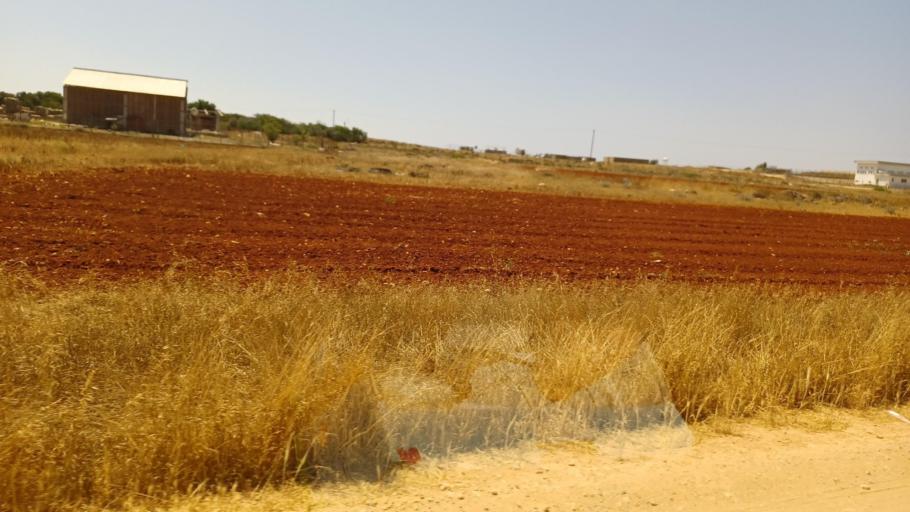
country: CY
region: Ammochostos
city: Liopetri
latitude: 35.0279
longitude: 33.8880
